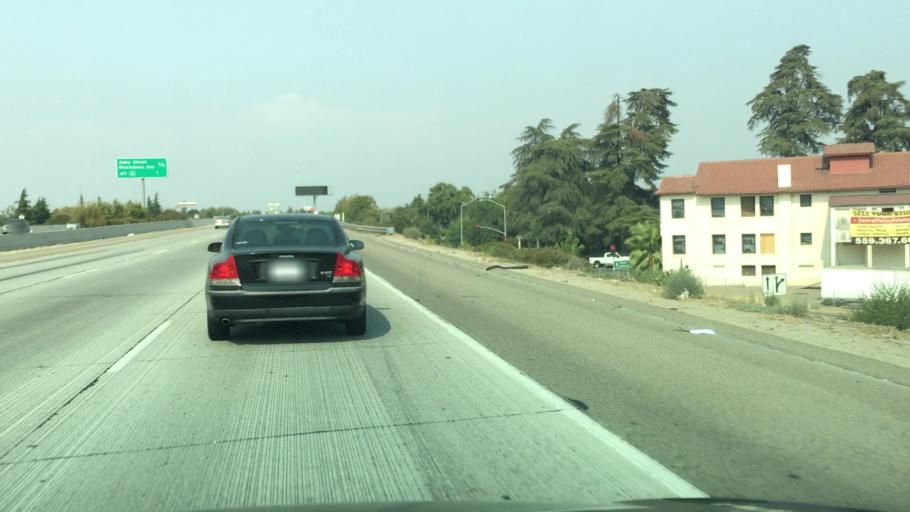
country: US
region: California
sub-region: Fresno County
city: Fresno
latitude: 36.7478
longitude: -119.8013
